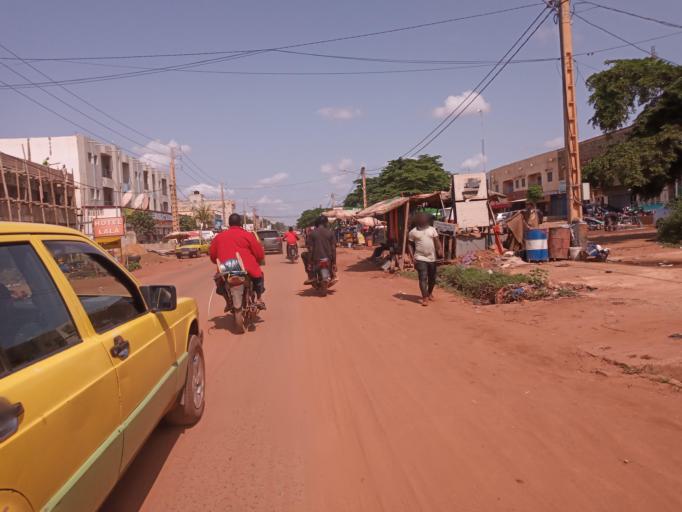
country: ML
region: Bamako
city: Bamako
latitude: 12.5975
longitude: -8.0226
